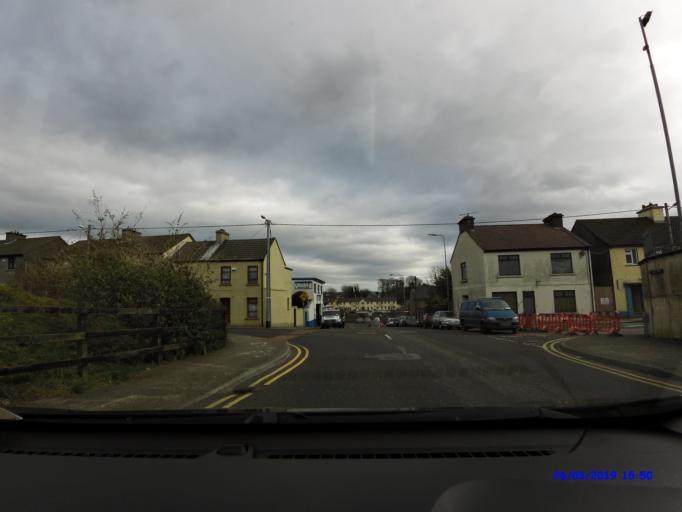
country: IE
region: Connaught
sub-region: Maigh Eo
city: Ballina
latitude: 54.1112
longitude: -9.1579
